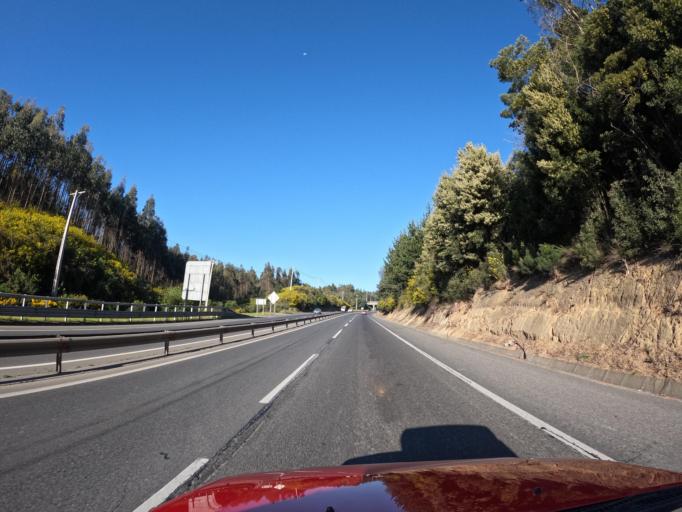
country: CL
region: Biobio
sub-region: Provincia de Concepcion
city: Penco
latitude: -36.7528
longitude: -72.9836
